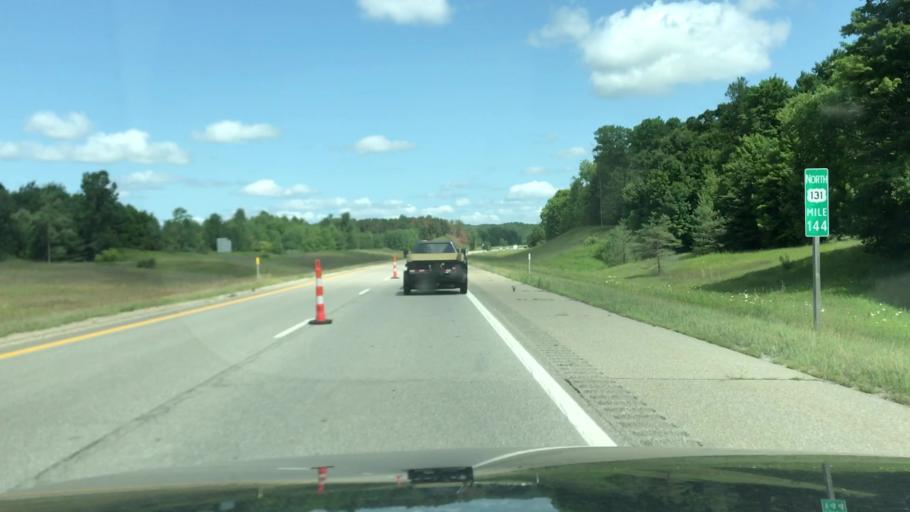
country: US
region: Michigan
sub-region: Mecosta County
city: Big Rapids
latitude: 43.7613
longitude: -85.5321
